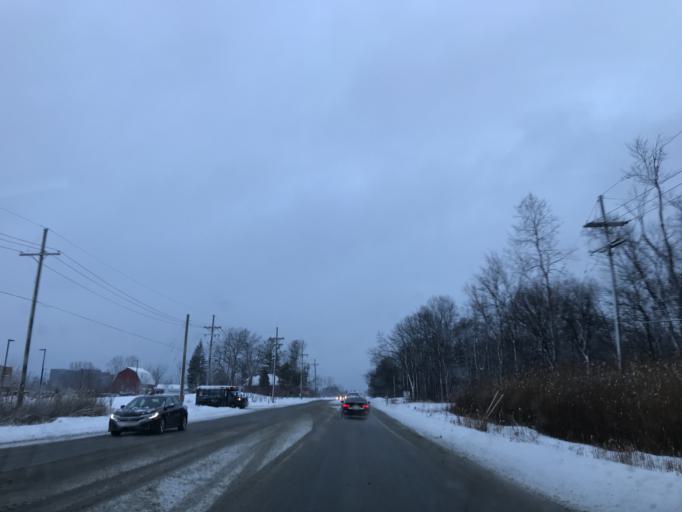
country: US
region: Michigan
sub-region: Oakland County
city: Novi
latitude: 42.4802
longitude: -83.5152
